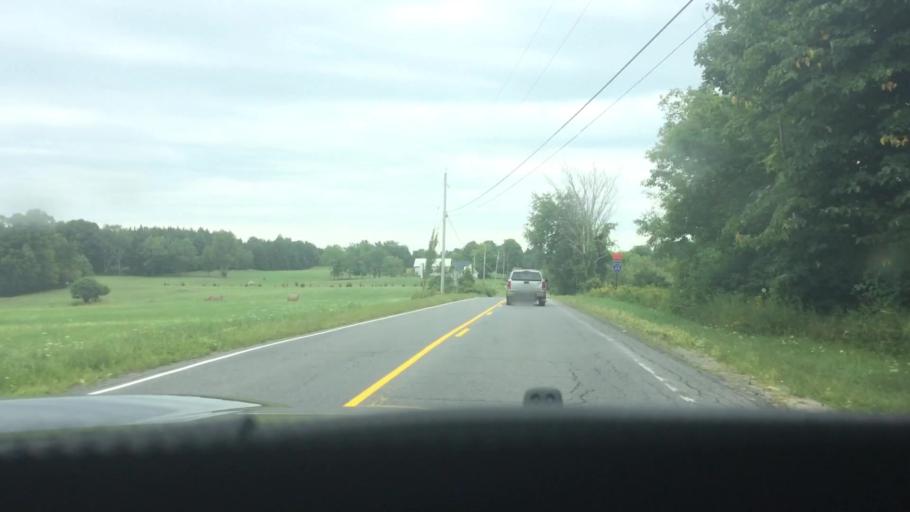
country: US
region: New York
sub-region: St. Lawrence County
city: Canton
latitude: 44.5280
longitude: -75.1885
